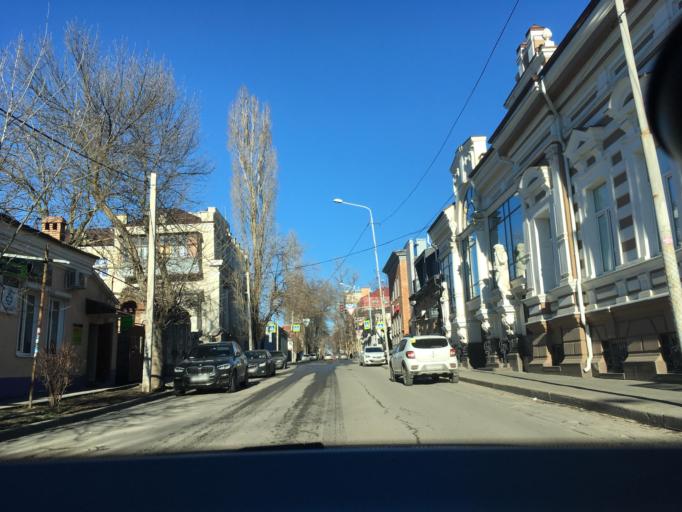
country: RU
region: Rostov
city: Rostov-na-Donu
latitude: 47.2307
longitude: 39.7571
